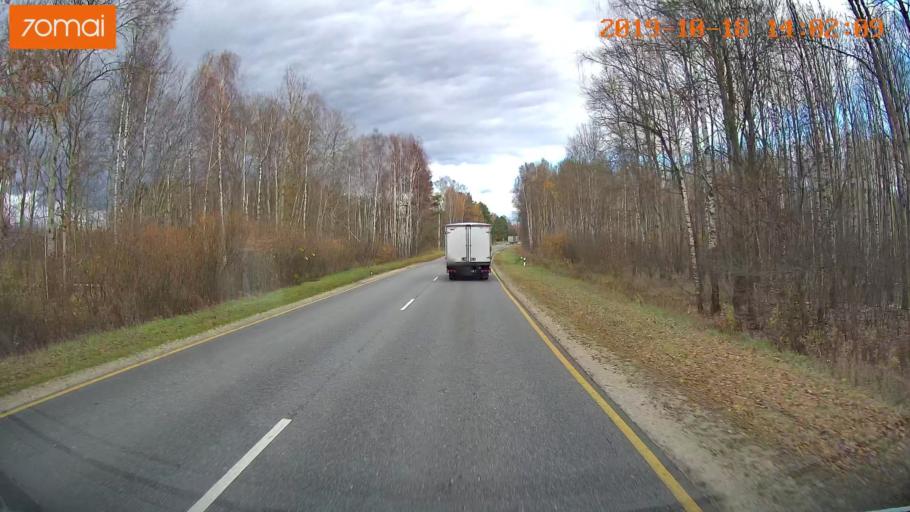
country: RU
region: Rjazan
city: Spas-Klepiki
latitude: 55.1117
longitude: 40.1023
